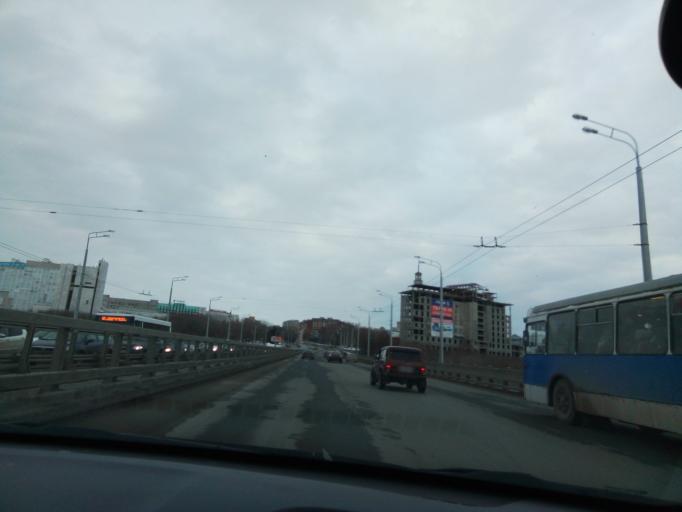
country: RU
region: Chuvashia
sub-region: Cheboksarskiy Rayon
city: Cheboksary
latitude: 56.1447
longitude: 47.2437
